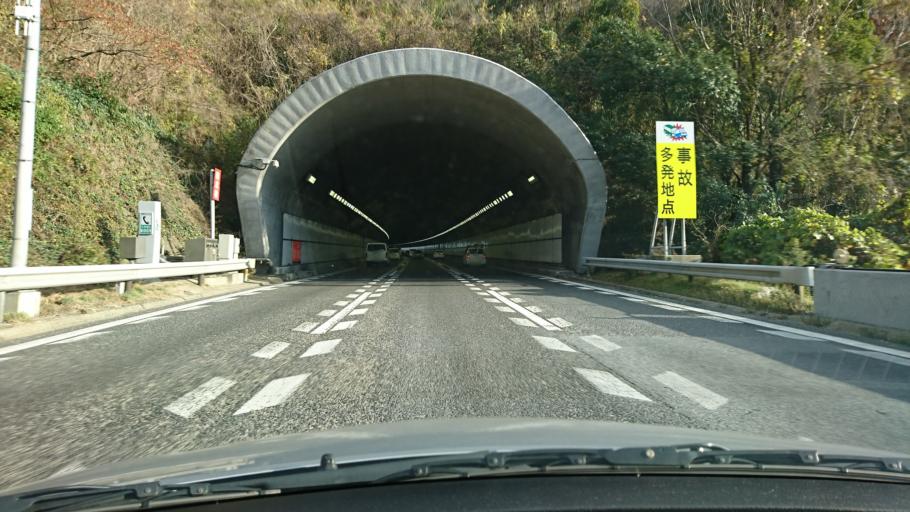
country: JP
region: Hyogo
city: Takarazuka
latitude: 34.8209
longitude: 135.3351
